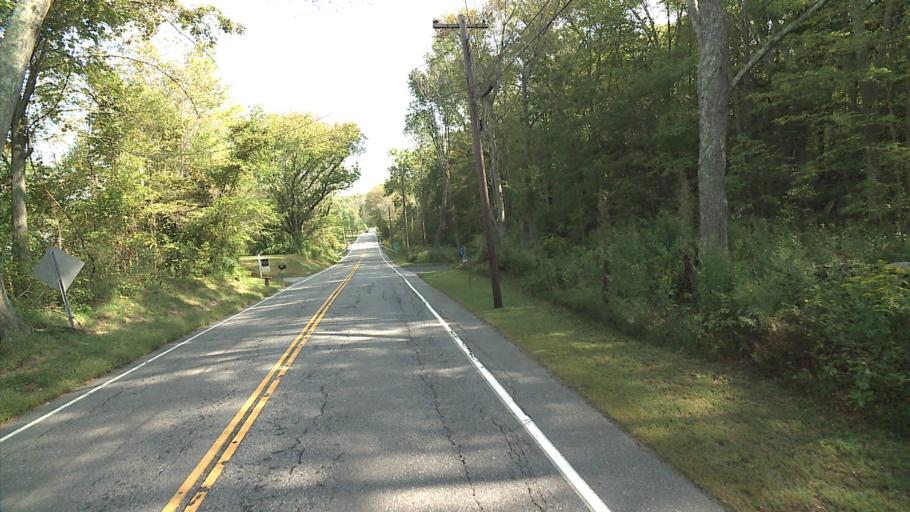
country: US
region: Connecticut
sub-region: New London County
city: Jewett City
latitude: 41.6401
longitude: -71.9923
